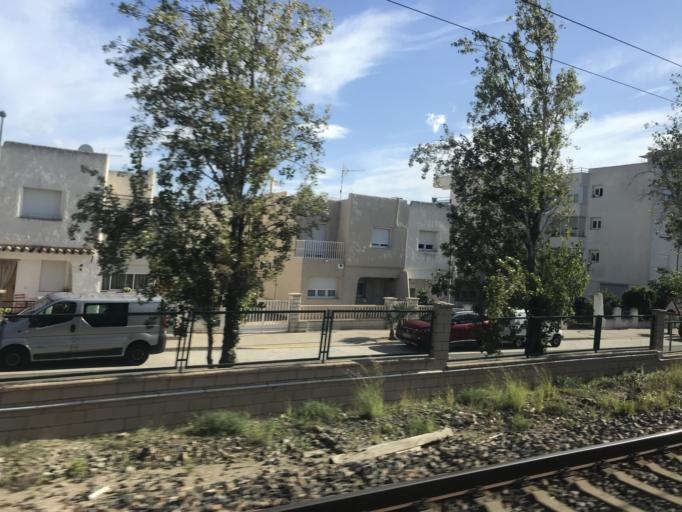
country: ES
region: Catalonia
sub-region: Provincia de Tarragona
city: L'Ampolla
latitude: 40.8156
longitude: 0.7144
